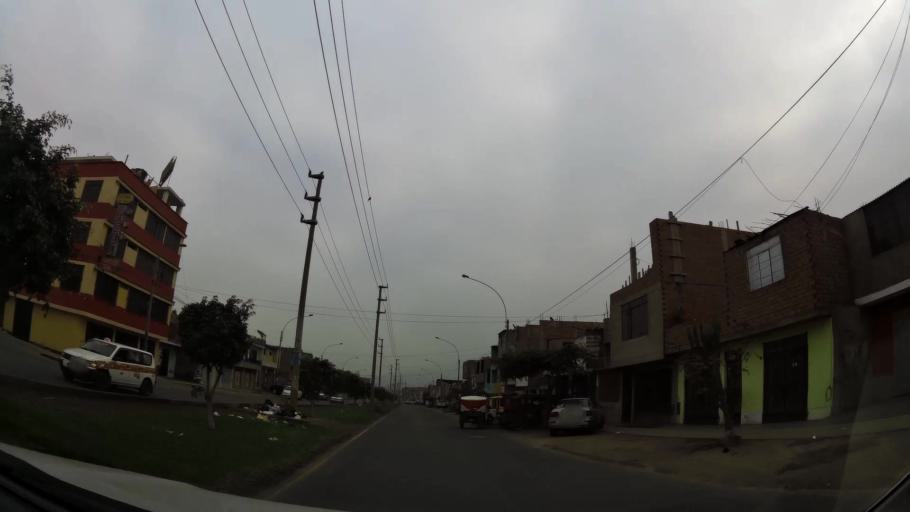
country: PE
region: Lima
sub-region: Lima
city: Independencia
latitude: -11.9682
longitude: -76.9976
